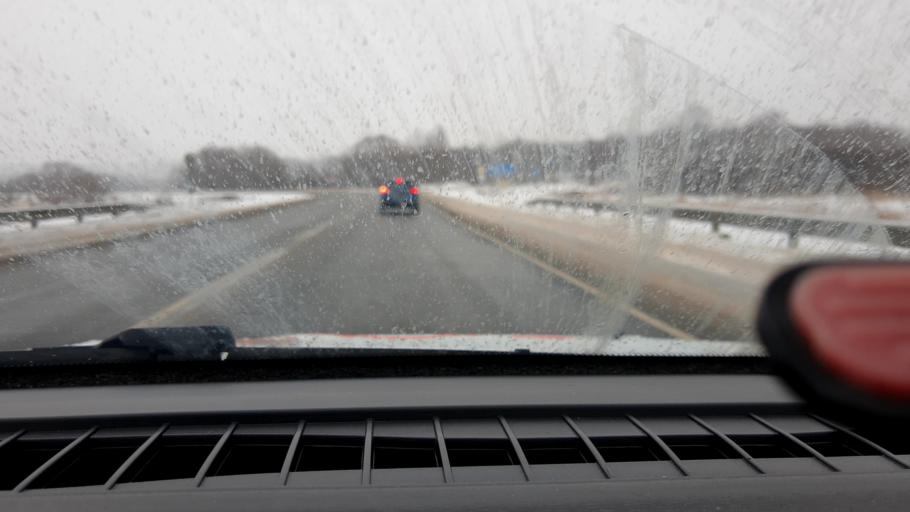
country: RU
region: Nizjnij Novgorod
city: Kstovo
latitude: 56.1138
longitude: 44.1985
